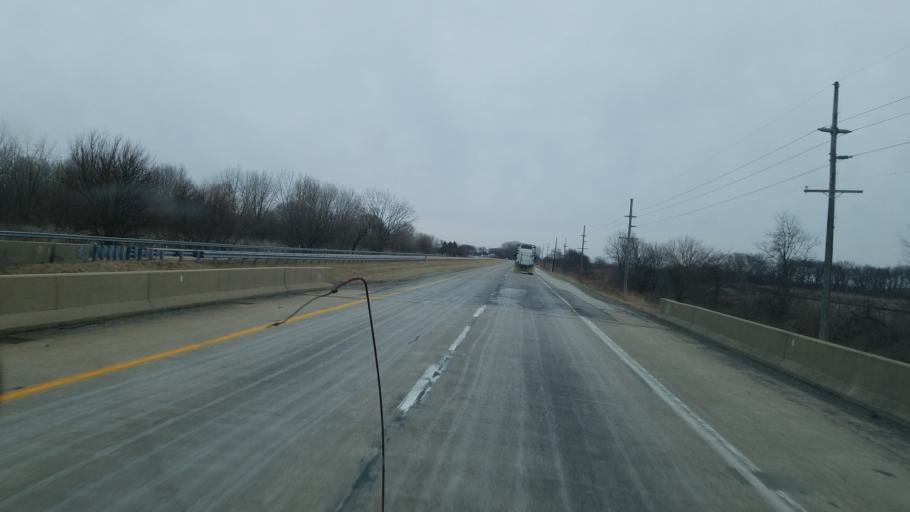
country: US
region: Indiana
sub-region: LaPorte County
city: Kingsford Heights
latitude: 41.3951
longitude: -86.6676
